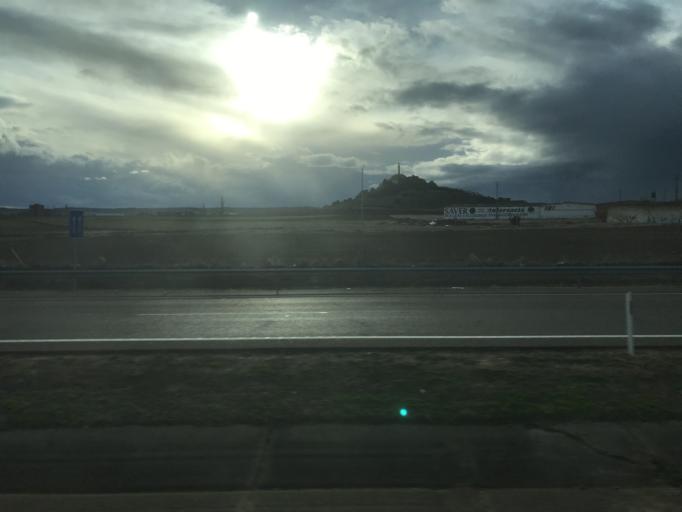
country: ES
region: Castille and Leon
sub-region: Provincia de Palencia
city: Villalobon
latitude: 42.0297
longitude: -4.5166
